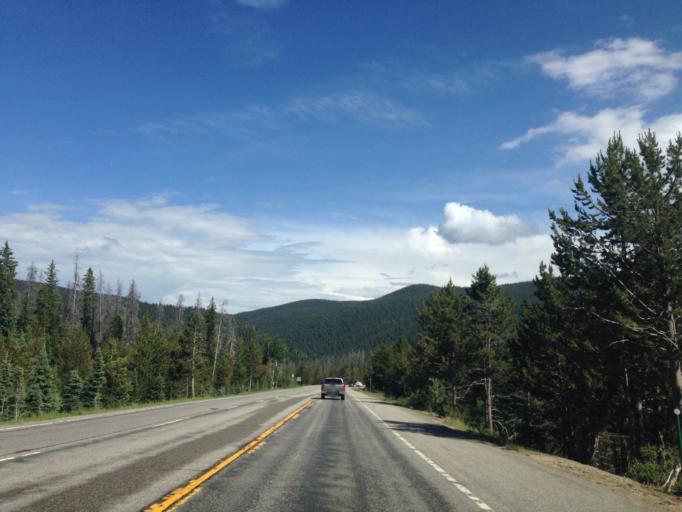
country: US
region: Colorado
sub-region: Routt County
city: Steamboat Springs
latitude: 40.3535
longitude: -106.7471
